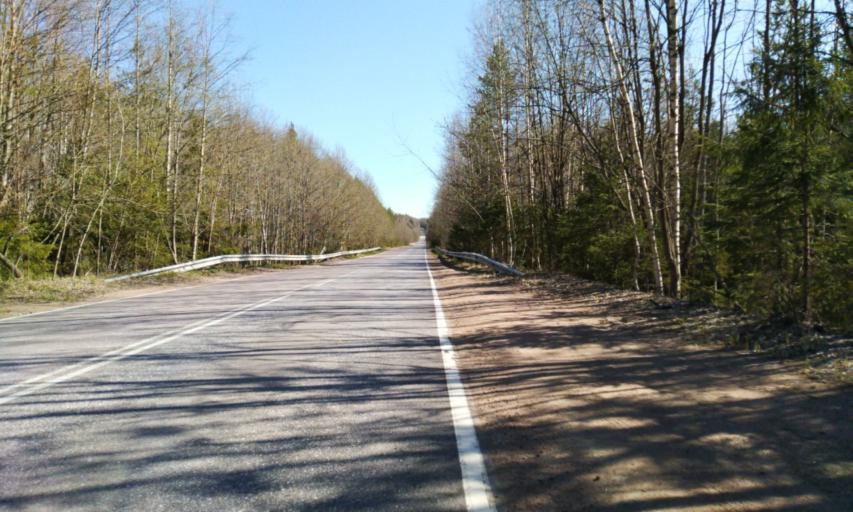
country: RU
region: Leningrad
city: Garbolovo
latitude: 60.3774
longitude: 30.4592
